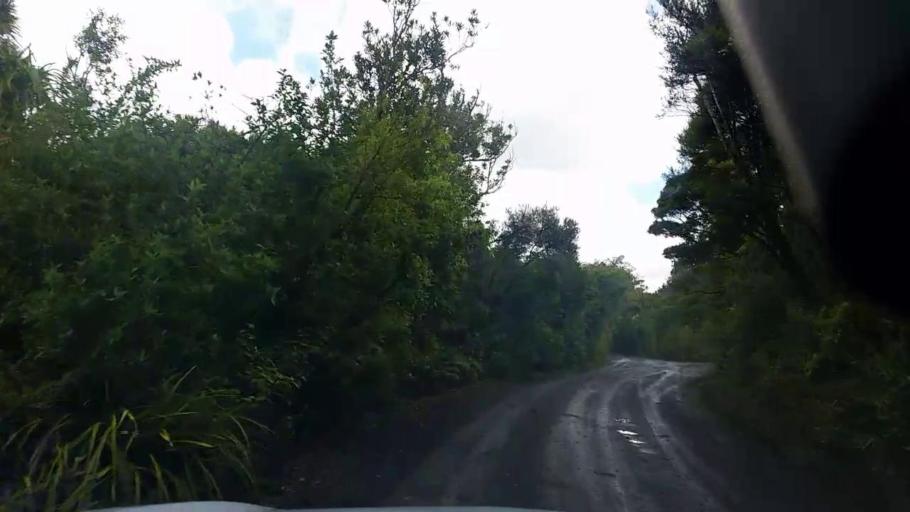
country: NZ
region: Auckland
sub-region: Auckland
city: Muriwai Beach
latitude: -36.9266
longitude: 174.4986
